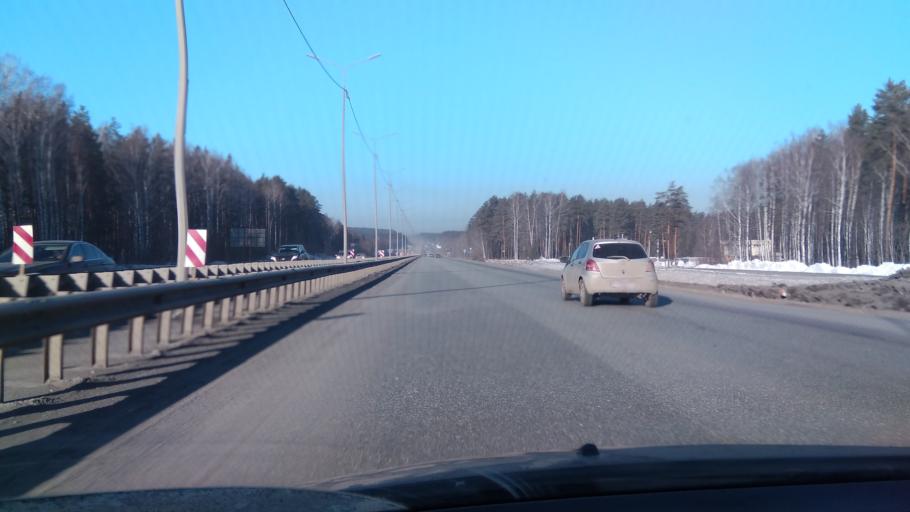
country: RU
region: Sverdlovsk
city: Shirokaya Rechka
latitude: 56.8270
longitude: 60.4357
